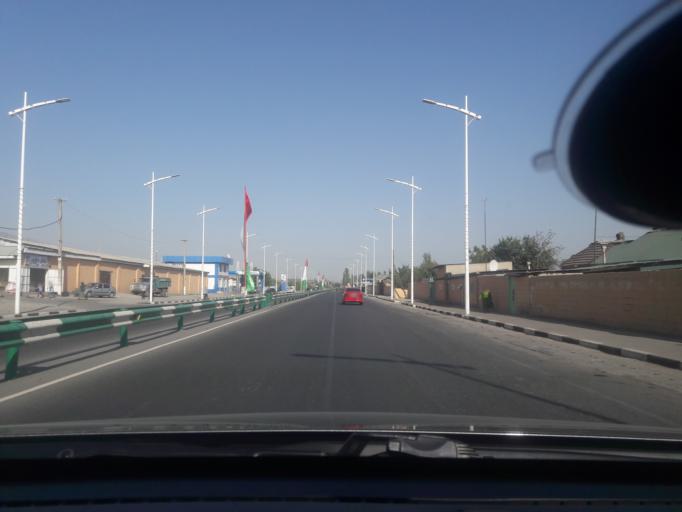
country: TJ
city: Shahrinav
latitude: 38.5766
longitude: 68.3330
